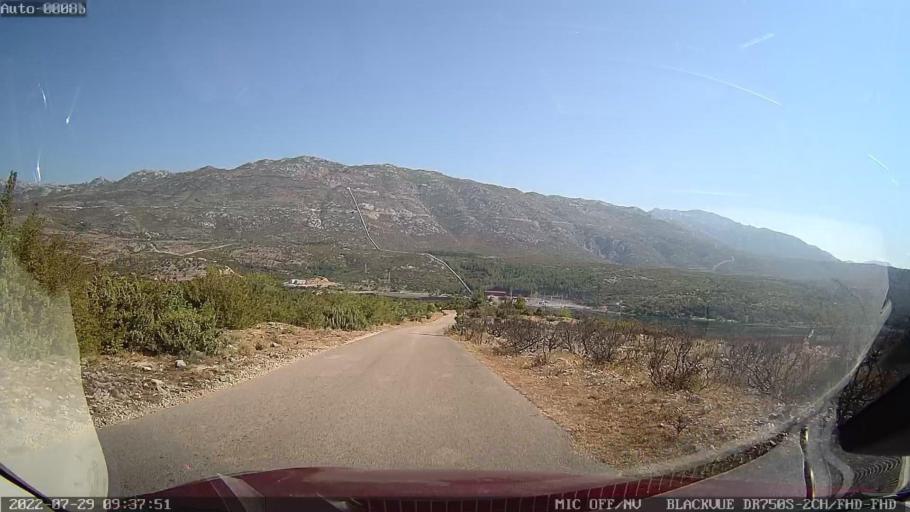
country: HR
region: Zadarska
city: Obrovac
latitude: 44.1987
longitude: 15.7469
